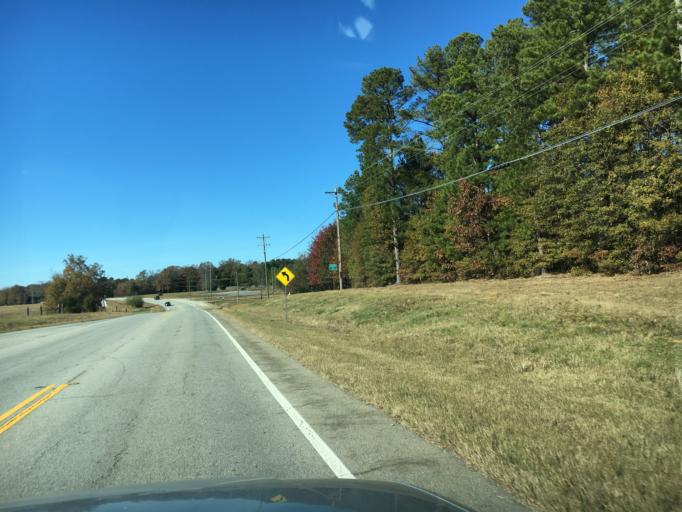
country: US
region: Georgia
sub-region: Hart County
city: Hartwell
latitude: 34.3400
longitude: -82.8467
